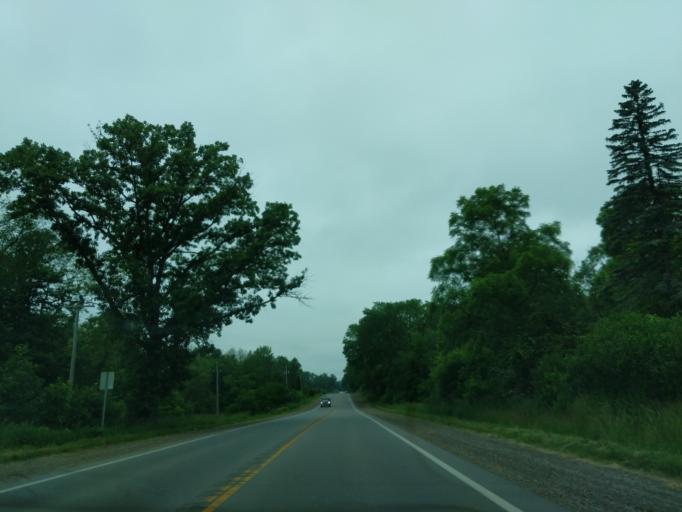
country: US
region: Michigan
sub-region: Branch County
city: Quincy
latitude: 41.9514
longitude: -84.7974
